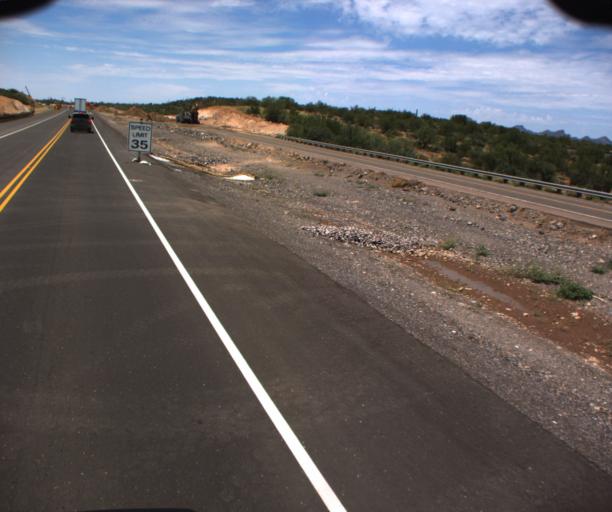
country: US
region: Arizona
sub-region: Pinal County
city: Superior
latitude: 33.2836
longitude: -111.1381
